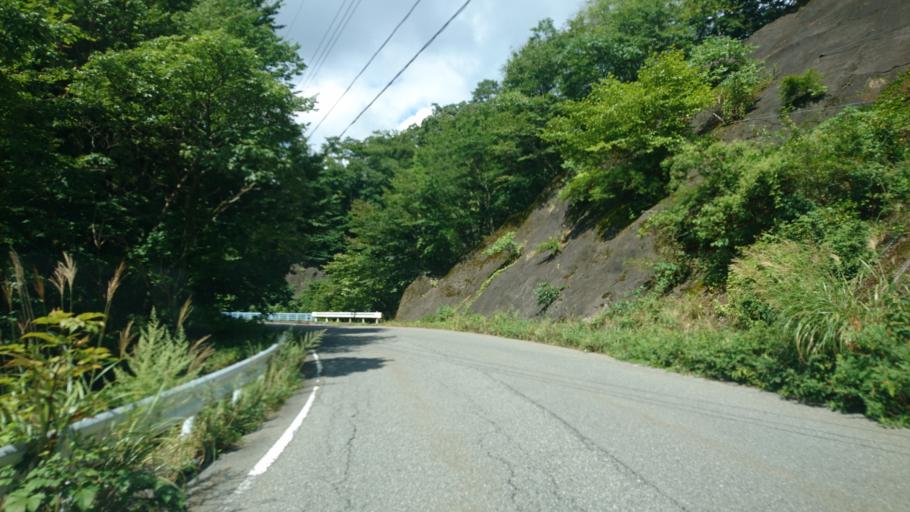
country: JP
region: Gunma
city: Omamacho-omama
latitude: 36.5670
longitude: 139.2426
